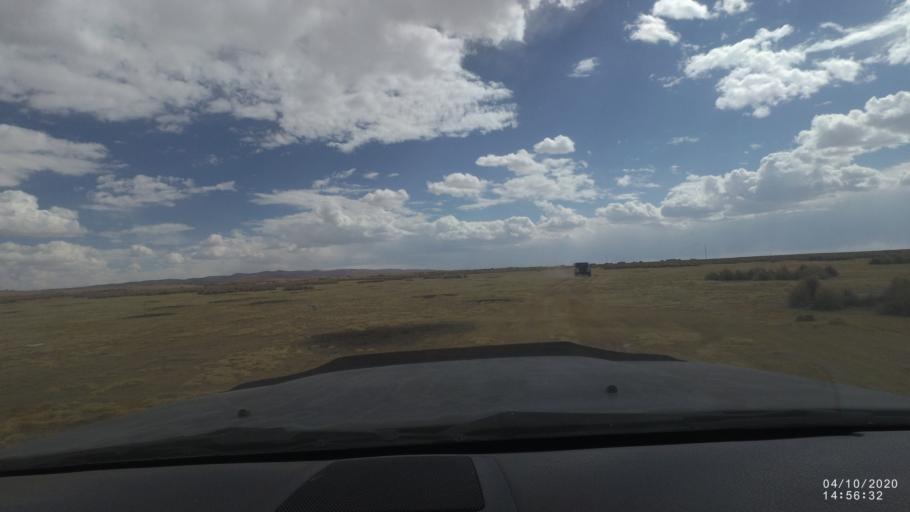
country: BO
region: Oruro
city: Poopo
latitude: -18.6846
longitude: -67.5162
